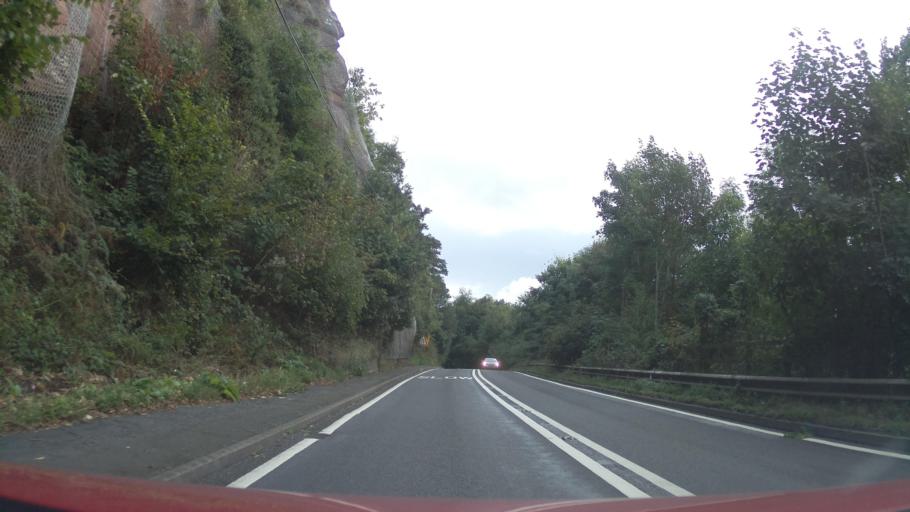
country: GB
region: England
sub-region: Shropshire
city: Bridgnorth
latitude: 52.5441
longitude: -2.4088
